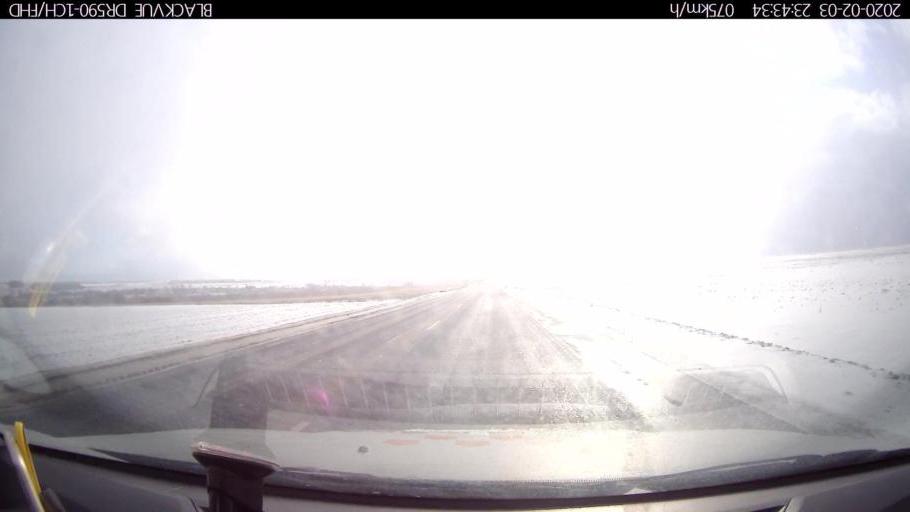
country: RU
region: Nizjnij Novgorod
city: Dal'neye Konstantinovo
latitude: 55.8390
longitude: 44.1256
